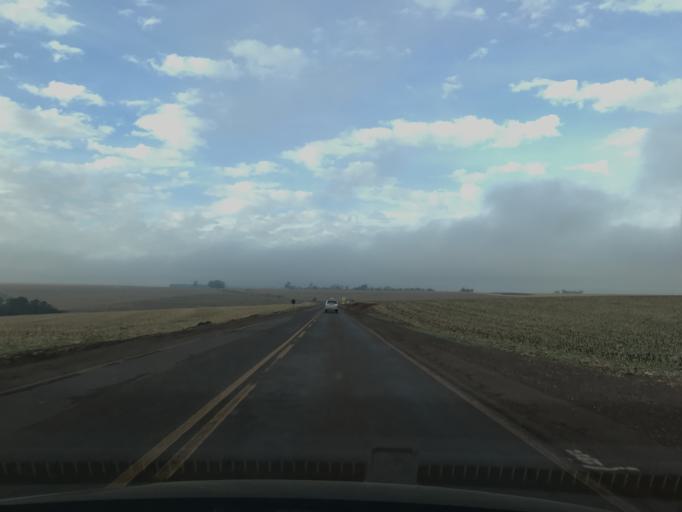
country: BR
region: Parana
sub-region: Toledo
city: Toledo
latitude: -24.5827
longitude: -53.7225
